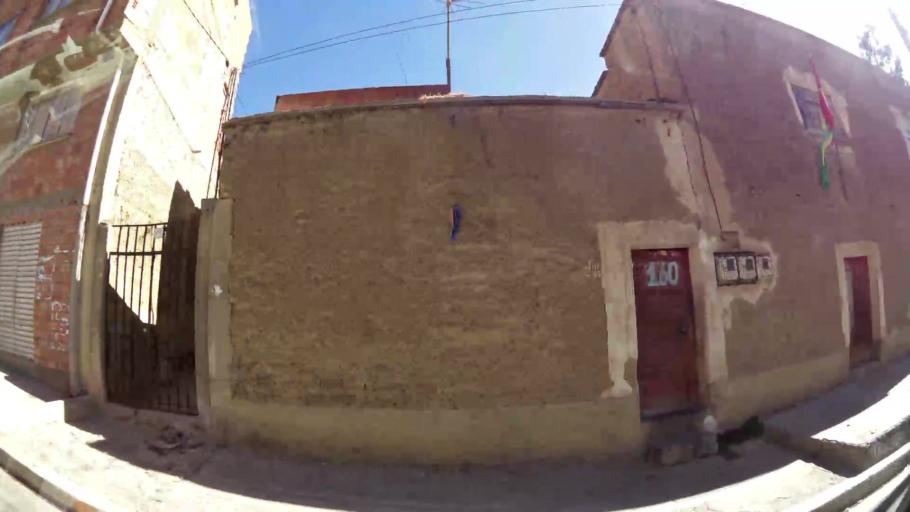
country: BO
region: La Paz
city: La Paz
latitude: -16.5050
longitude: -68.1488
